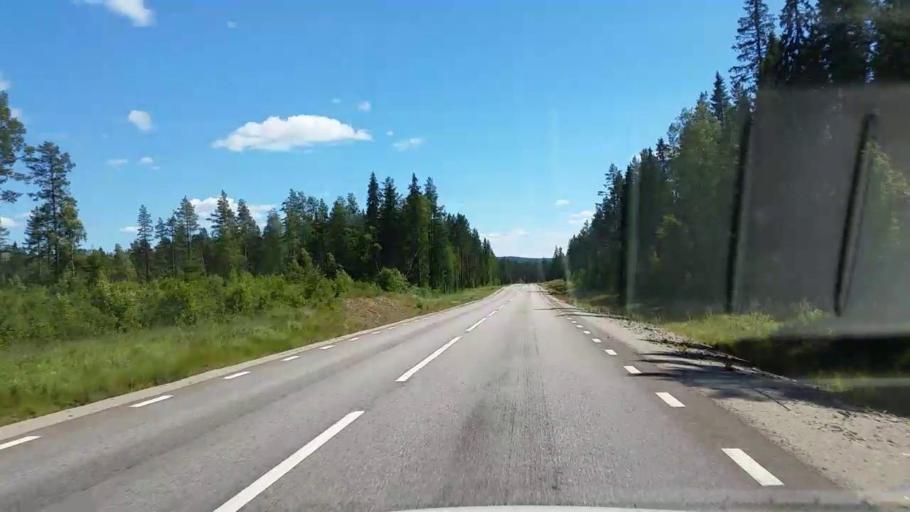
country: SE
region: Gaevleborg
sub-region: Bollnas Kommun
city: Vittsjo
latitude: 61.0641
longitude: 15.7995
